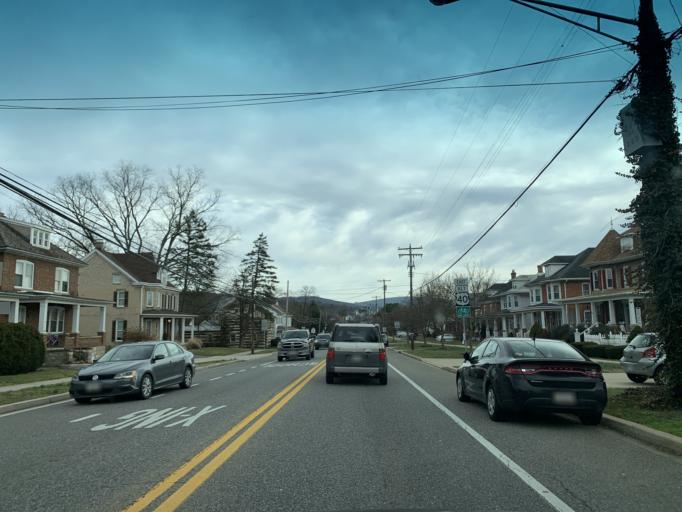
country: US
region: Maryland
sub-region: Washington County
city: Boonsboro
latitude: 39.5124
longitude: -77.6556
